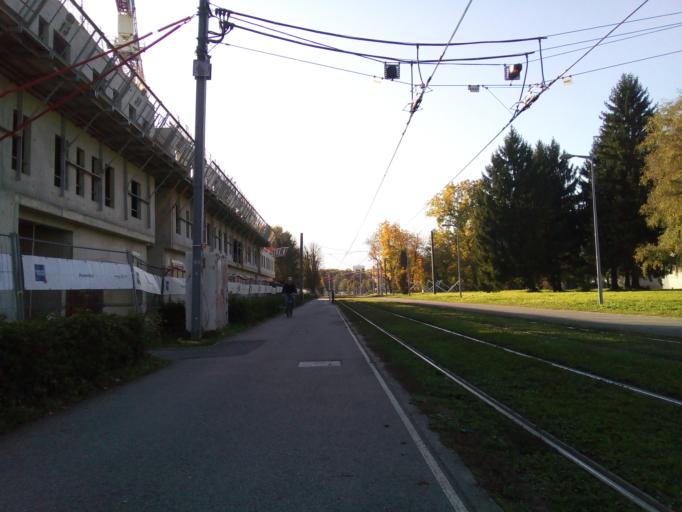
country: FR
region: Rhone-Alpes
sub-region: Departement de l'Isere
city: Corenc
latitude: 45.1921
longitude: 5.7616
